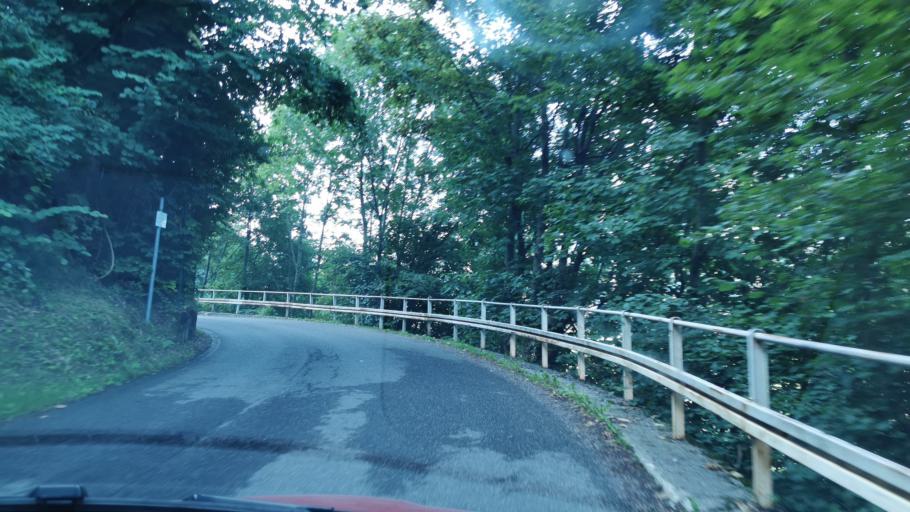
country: IT
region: Lombardy
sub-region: Provincia di Lecco
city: Moggio
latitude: 45.9220
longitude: 9.4890
